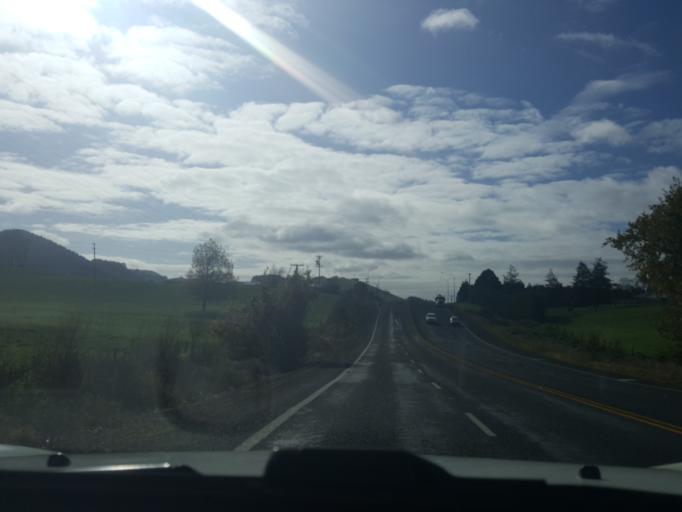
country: NZ
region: Waikato
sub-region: Hauraki District
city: Waihi
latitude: -37.4090
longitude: 175.8025
